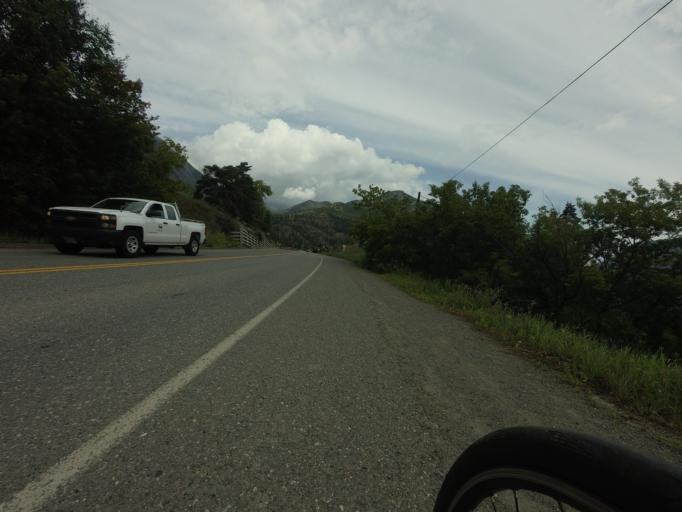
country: CA
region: British Columbia
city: Lillooet
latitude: 50.6841
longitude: -121.9340
